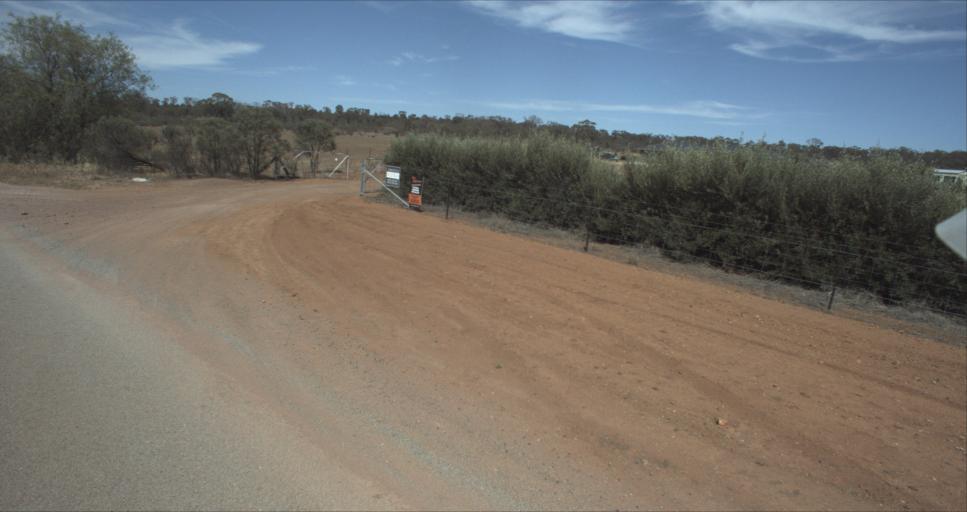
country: AU
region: New South Wales
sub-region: Leeton
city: Leeton
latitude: -34.5782
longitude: 146.4553
